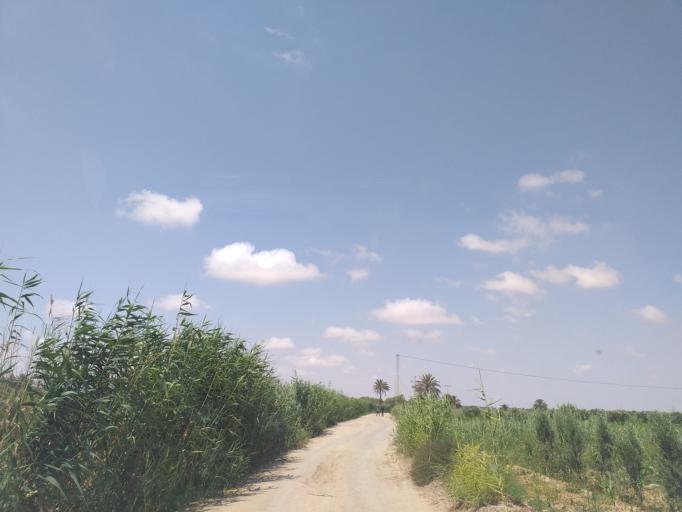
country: TN
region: Qabis
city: Gabes
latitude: 33.9534
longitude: 10.0468
